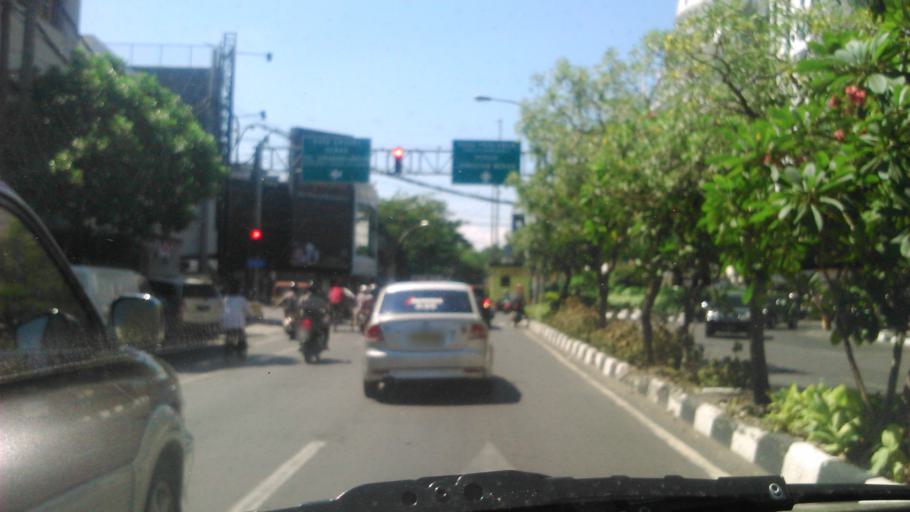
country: ID
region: East Java
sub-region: Kota Surabaya
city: Surabaya
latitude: -7.2591
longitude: 112.7329
